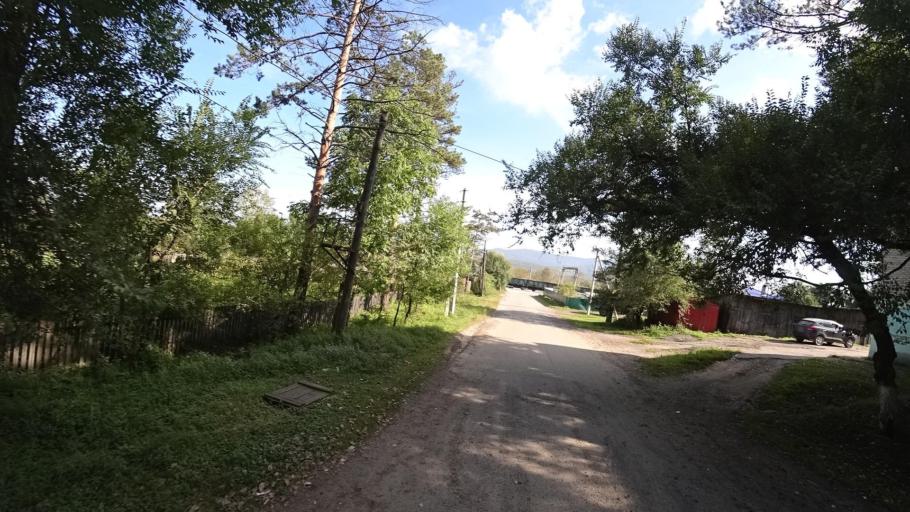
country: RU
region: Jewish Autonomous Oblast
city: Birakan
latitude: 48.9935
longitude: 131.7209
